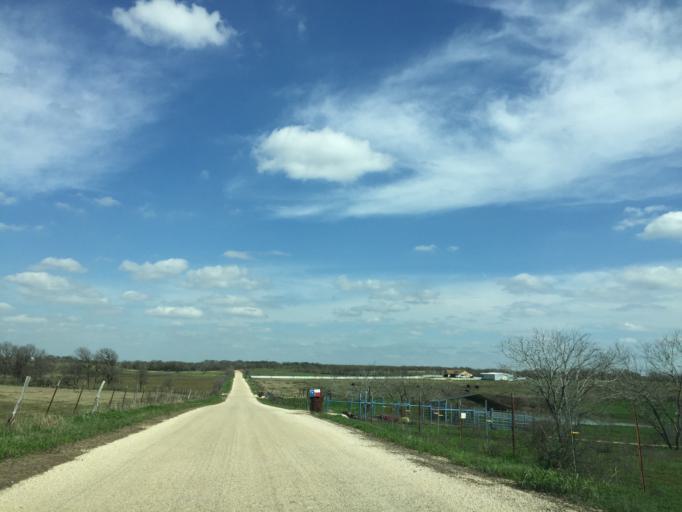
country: US
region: Texas
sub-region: Milam County
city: Thorndale
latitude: 30.5590
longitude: -97.2033
